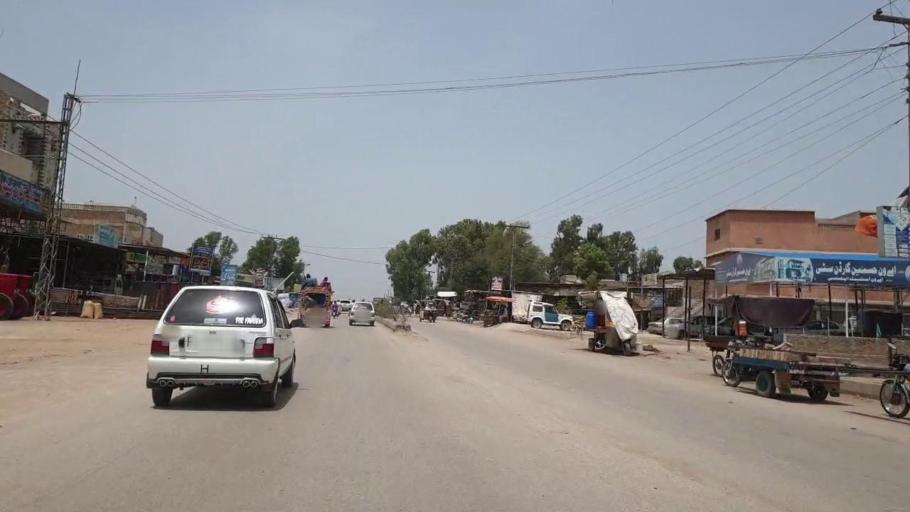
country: PK
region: Sindh
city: Nawabshah
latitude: 26.2527
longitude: 68.4210
